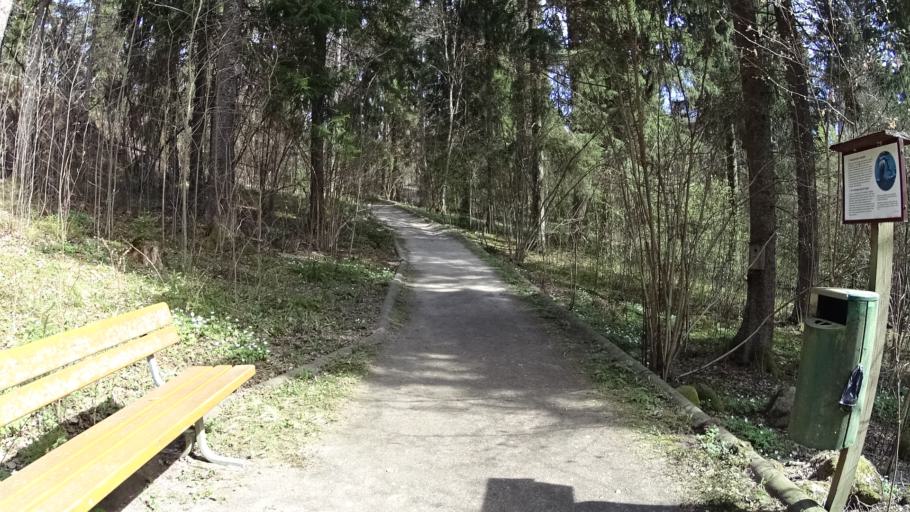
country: FI
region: Uusimaa
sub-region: Helsinki
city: Siuntio
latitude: 60.1674
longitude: 24.2130
